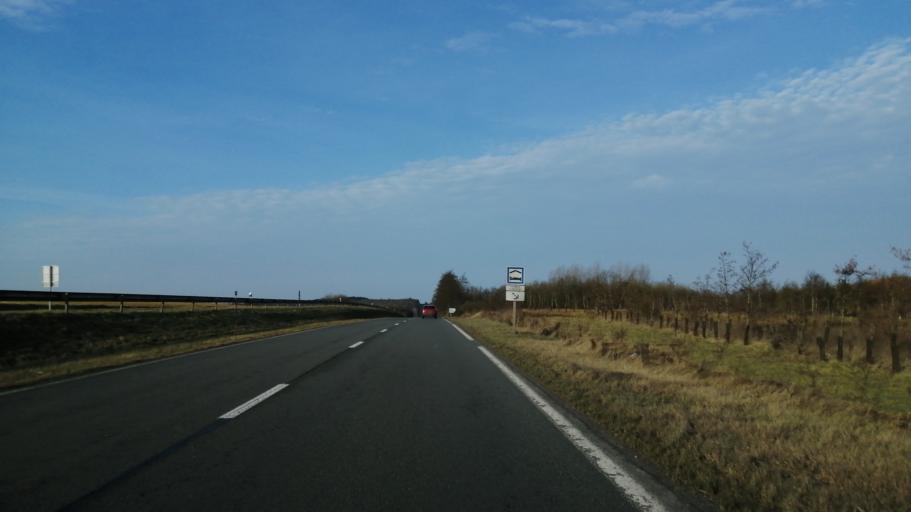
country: FR
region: Nord-Pas-de-Calais
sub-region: Departement du Pas-de-Calais
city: Rety
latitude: 50.7377
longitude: 1.7758
